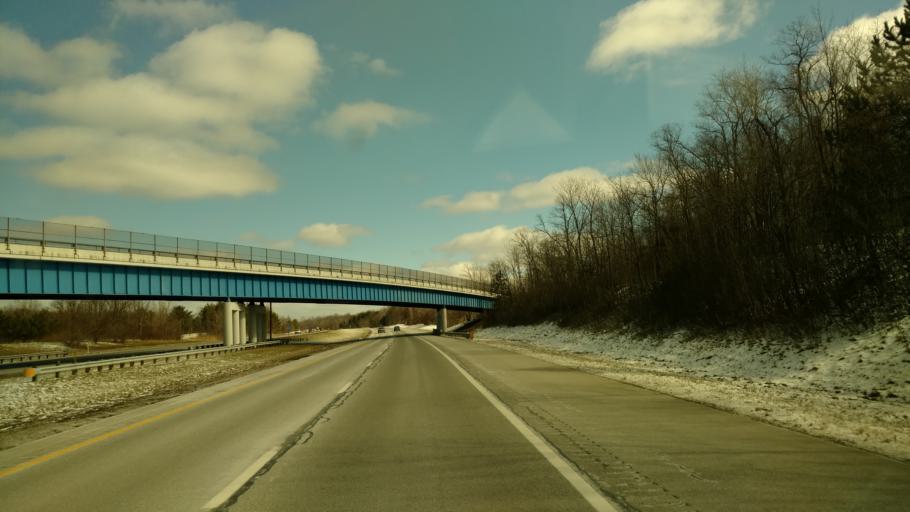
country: US
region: Ohio
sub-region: Lake County
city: Perry
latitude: 41.7221
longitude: -81.1264
